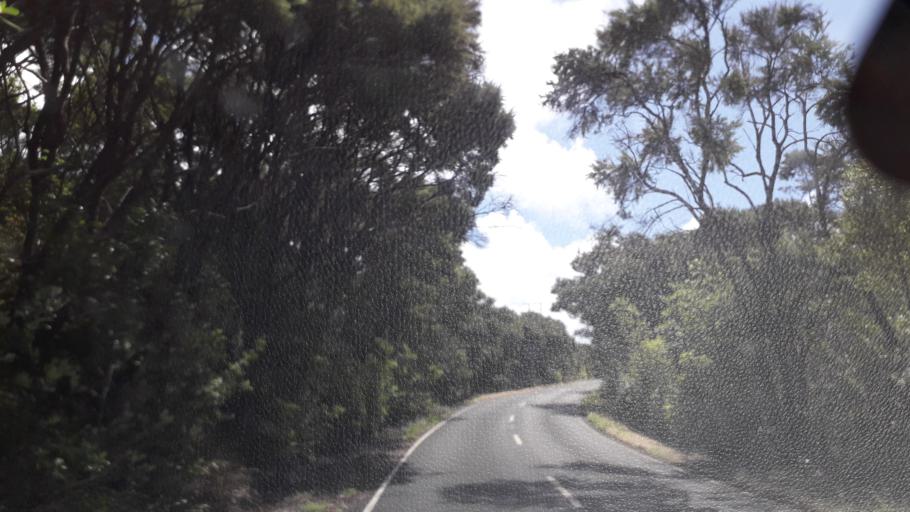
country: NZ
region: Northland
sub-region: Far North District
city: Paihia
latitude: -35.2446
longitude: 174.2508
